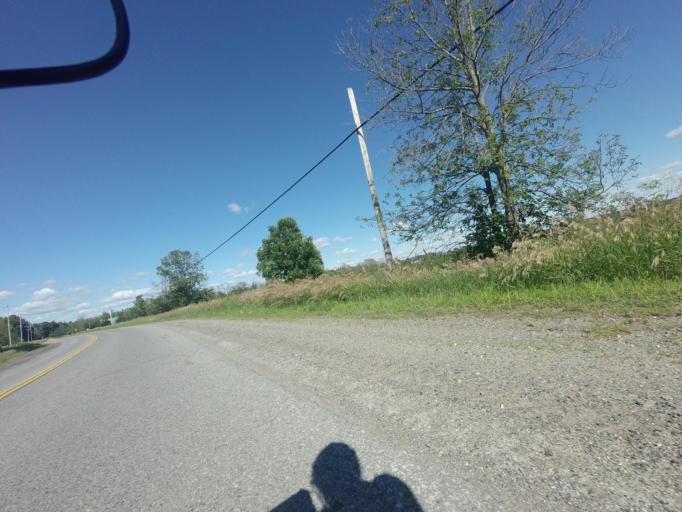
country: CA
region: Ontario
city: Arnprior
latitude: 45.4128
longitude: -76.4348
